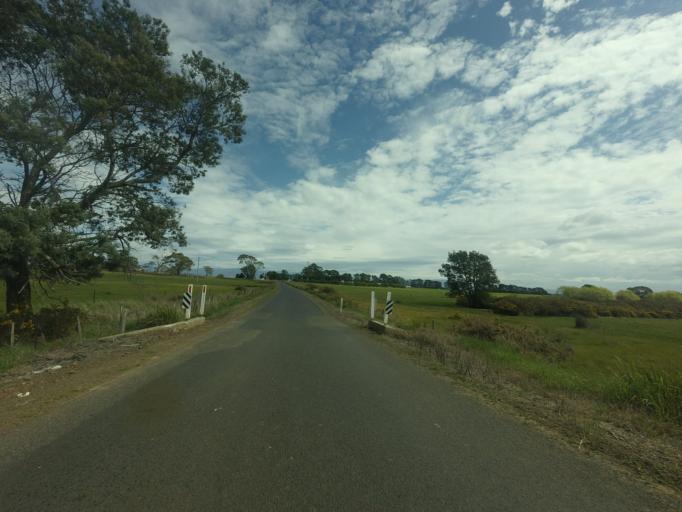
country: AU
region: Tasmania
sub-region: Northern Midlands
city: Longford
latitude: -41.7148
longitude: 147.1916
